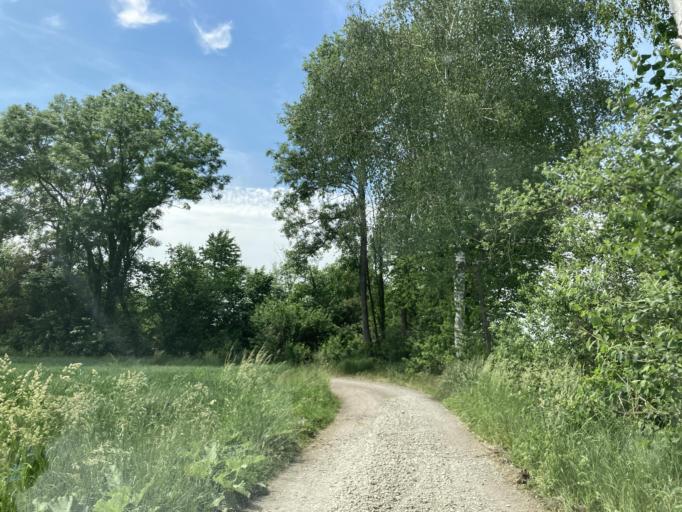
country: DE
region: Baden-Wuerttemberg
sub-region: Karlsruhe Region
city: Graben-Neudorf
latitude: 49.1738
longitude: 8.4504
